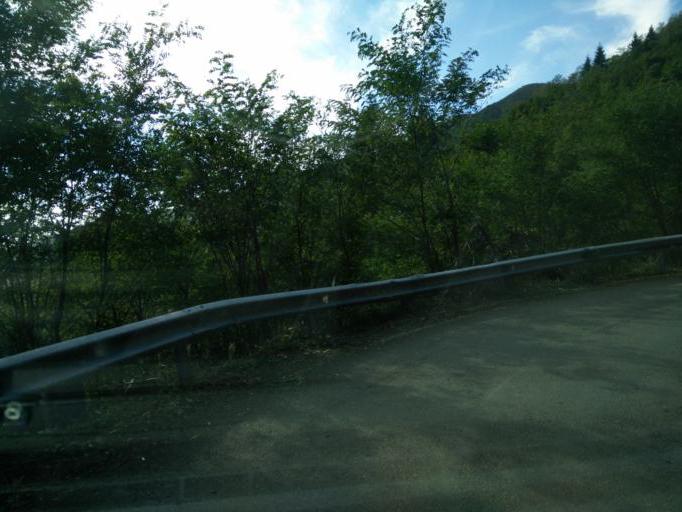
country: IT
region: Liguria
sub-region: Provincia di La Spezia
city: Sesta Godano
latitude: 44.3332
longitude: 9.7001
